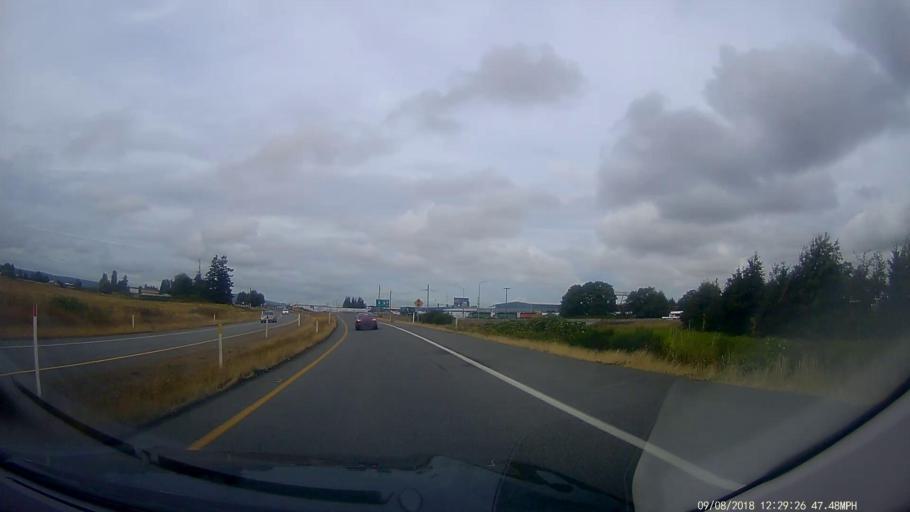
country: US
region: Washington
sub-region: Skagit County
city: Mount Vernon
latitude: 48.4452
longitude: -122.4291
